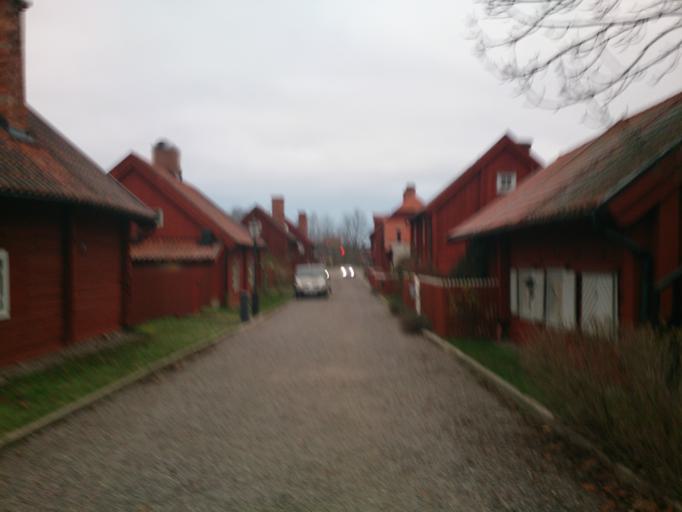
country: SE
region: OEstergoetland
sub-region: Atvidabergs Kommun
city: Atvidaberg
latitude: 58.1986
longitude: 16.0057
